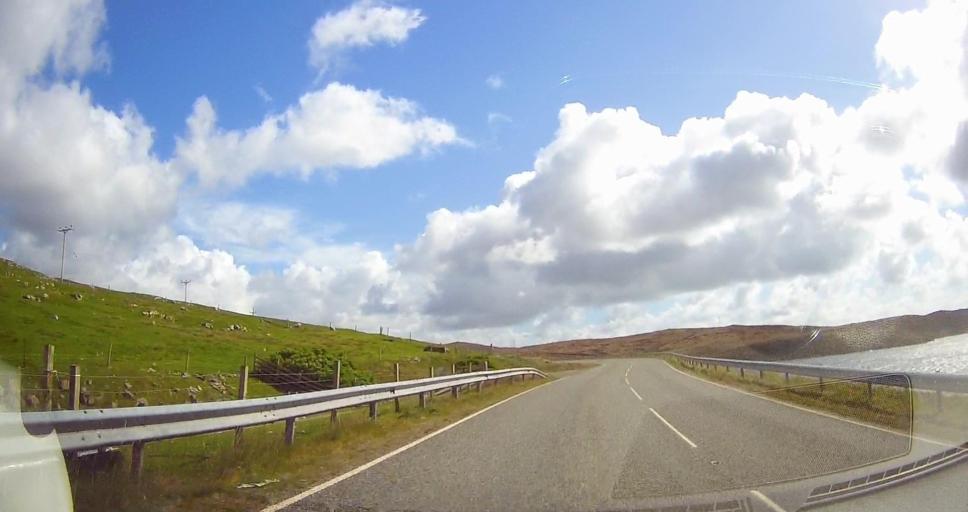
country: GB
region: Scotland
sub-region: Shetland Islands
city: Lerwick
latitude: 60.4645
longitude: -1.4049
